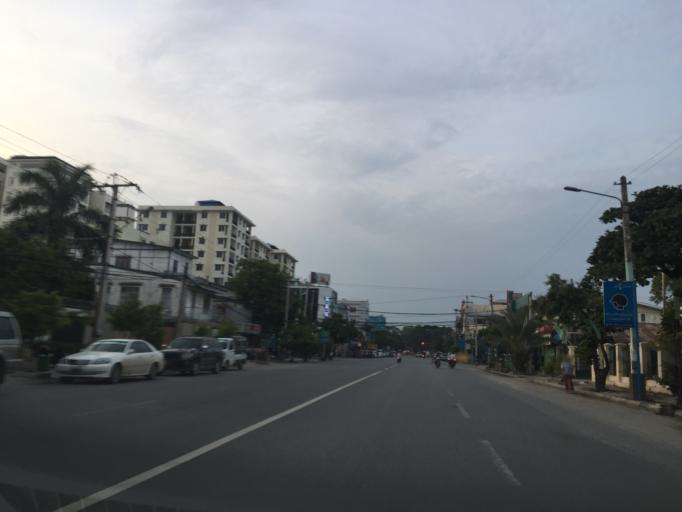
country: MM
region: Mandalay
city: Mandalay
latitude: 21.9802
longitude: 96.0958
